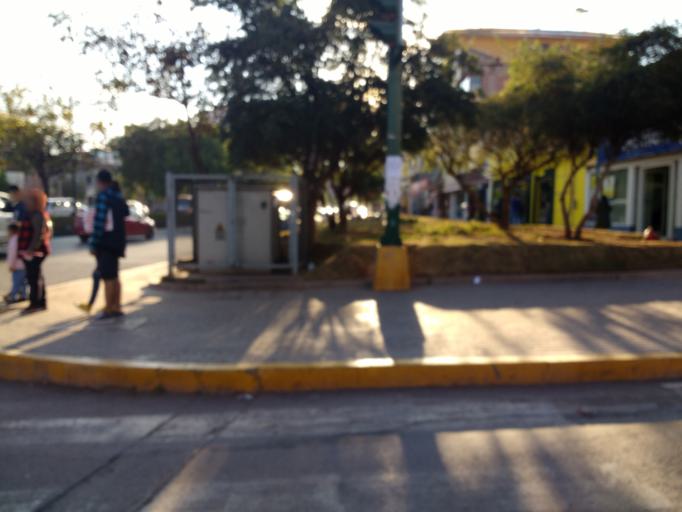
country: PE
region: Cusco
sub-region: Provincia de Cusco
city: Cusco
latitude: -13.5265
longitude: -71.9485
